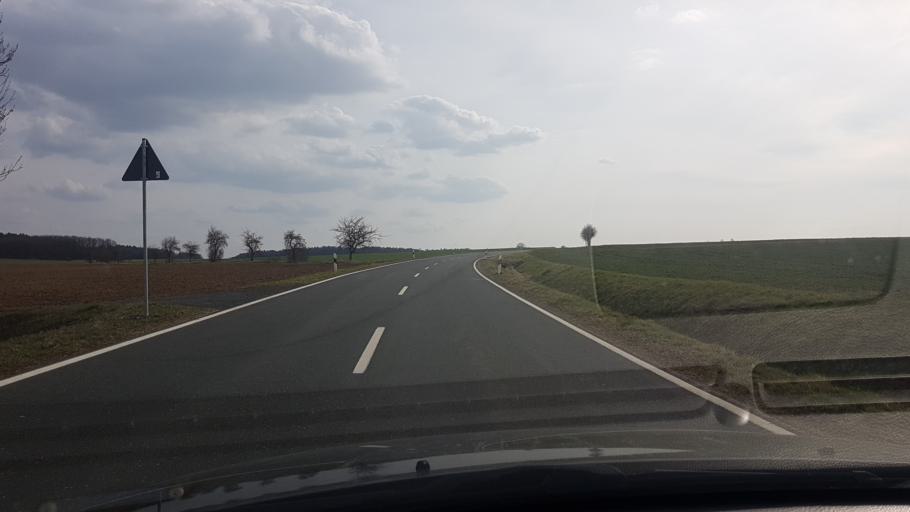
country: DE
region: Bavaria
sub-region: Upper Franconia
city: Schesslitz
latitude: 50.0299
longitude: 11.0076
